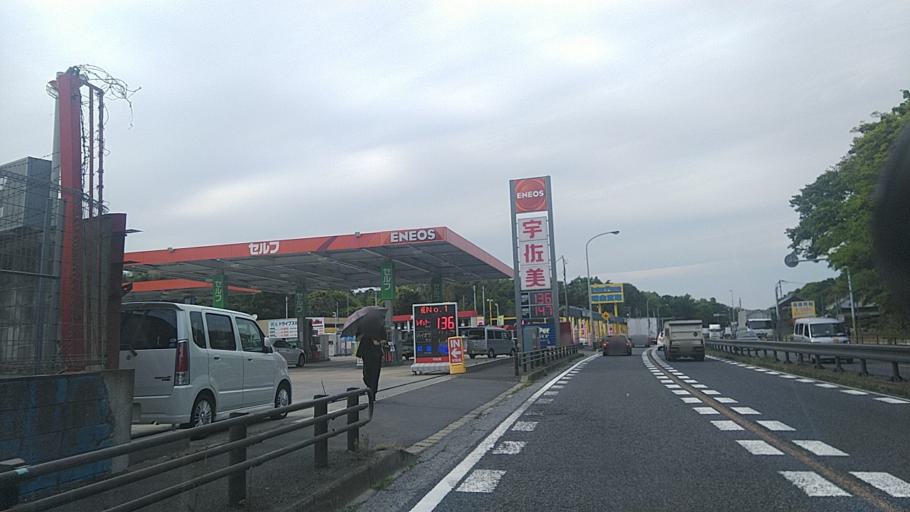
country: JP
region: Chiba
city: Yotsukaido
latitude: 35.6995
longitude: 140.1198
